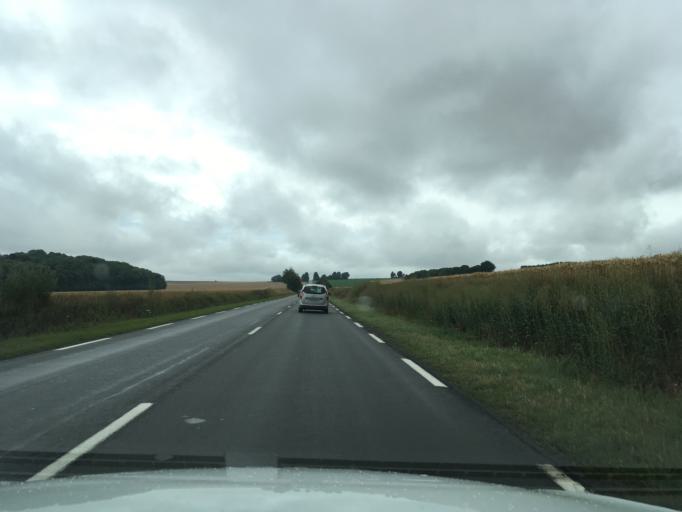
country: FR
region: Picardie
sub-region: Departement de l'Aisne
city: Homblieres
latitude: 49.8434
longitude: 3.4149
